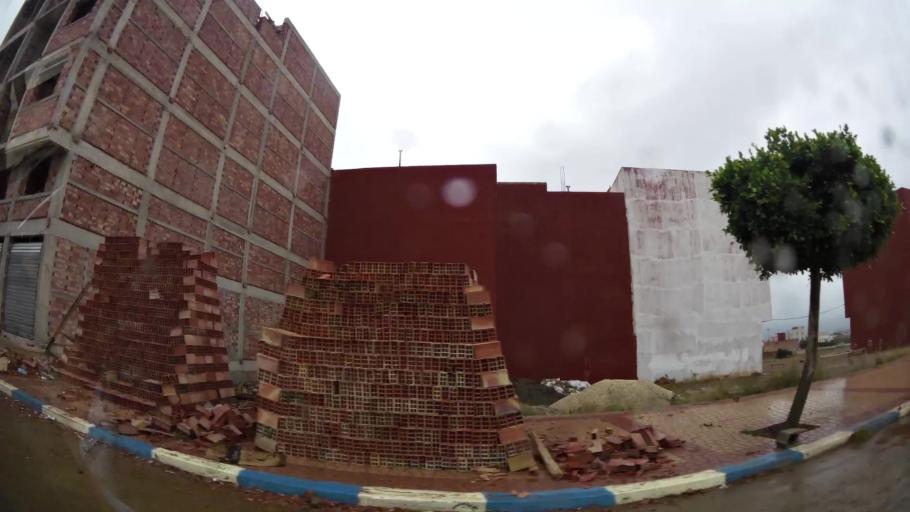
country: MA
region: Taza-Al Hoceima-Taounate
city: Imzourene
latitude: 35.1361
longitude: -3.8501
